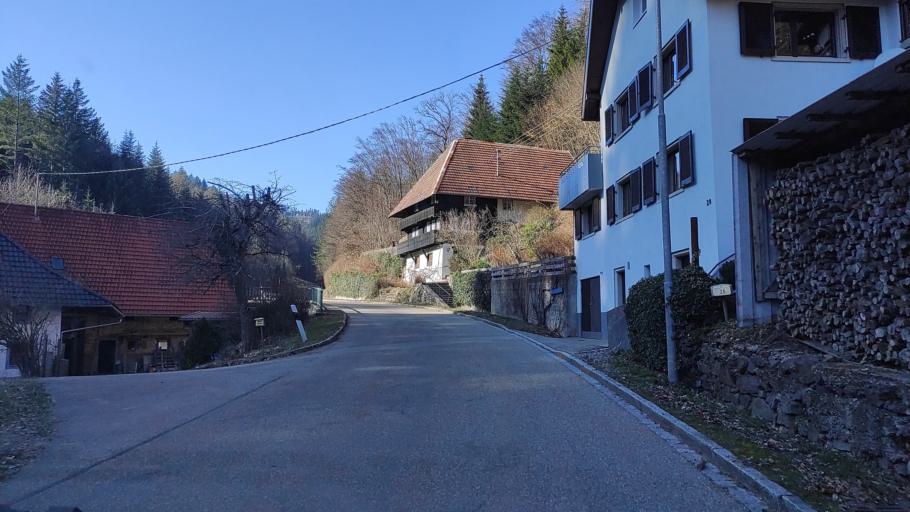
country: DE
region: Baden-Wuerttemberg
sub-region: Freiburg Region
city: Gutach im Breisgau
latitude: 48.1661
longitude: 8.0104
